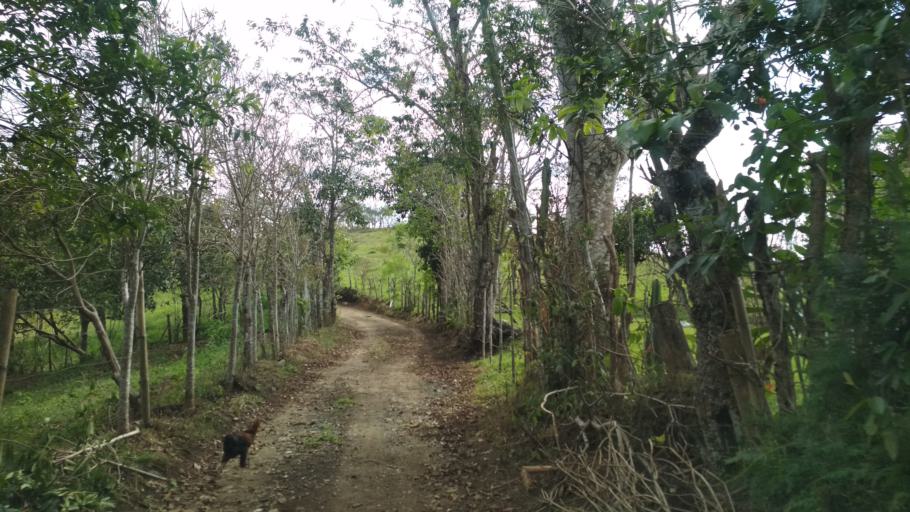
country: CO
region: Cauca
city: Lopez
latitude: 2.4037
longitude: -76.7135
